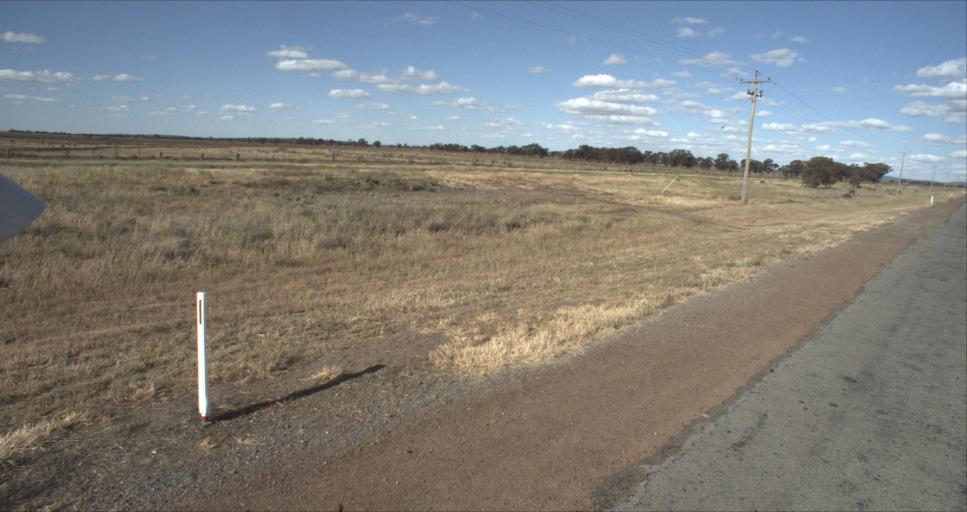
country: AU
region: New South Wales
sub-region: Leeton
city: Leeton
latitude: -34.4556
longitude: 146.2798
